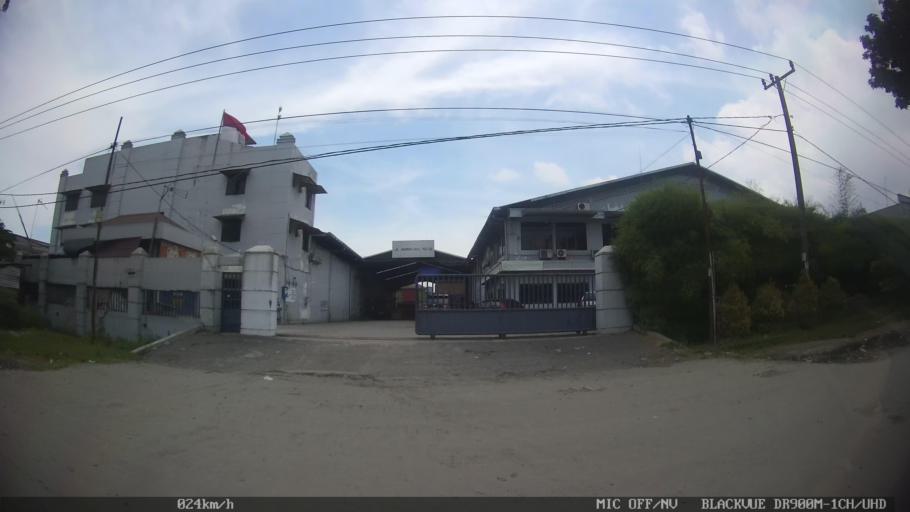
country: ID
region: North Sumatra
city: Labuhan Deli
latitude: 3.6773
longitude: 98.6856
